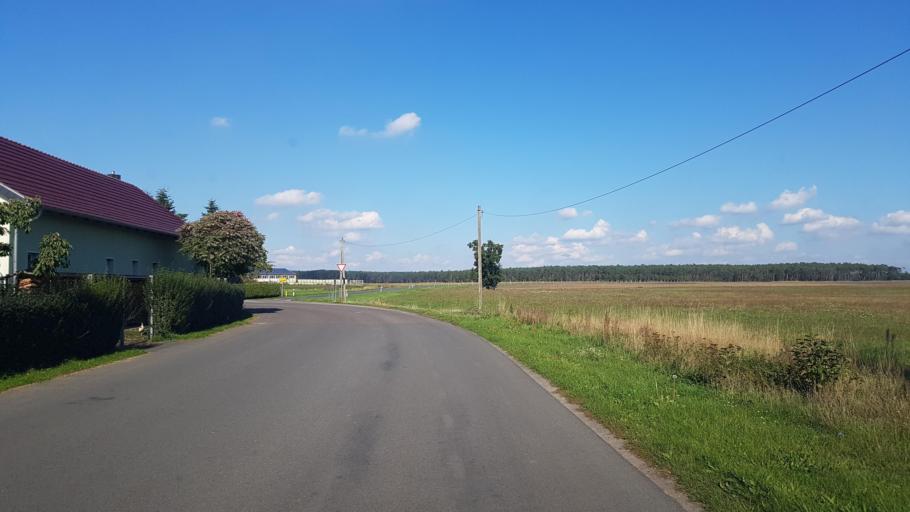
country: DE
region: Brandenburg
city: Ihlow
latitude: 51.8464
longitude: 13.2746
